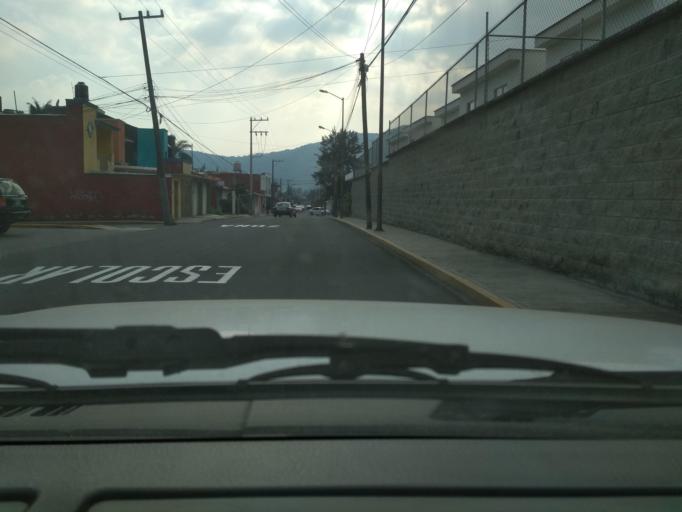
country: MX
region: Veracruz
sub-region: Mariano Escobedo
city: Palmira
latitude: 18.8700
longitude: -97.0972
